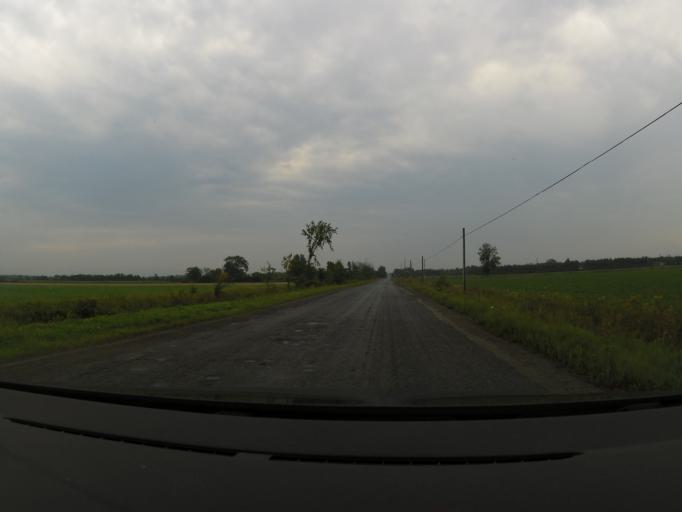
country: CA
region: Ontario
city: Carleton Place
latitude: 45.1829
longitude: -76.0892
